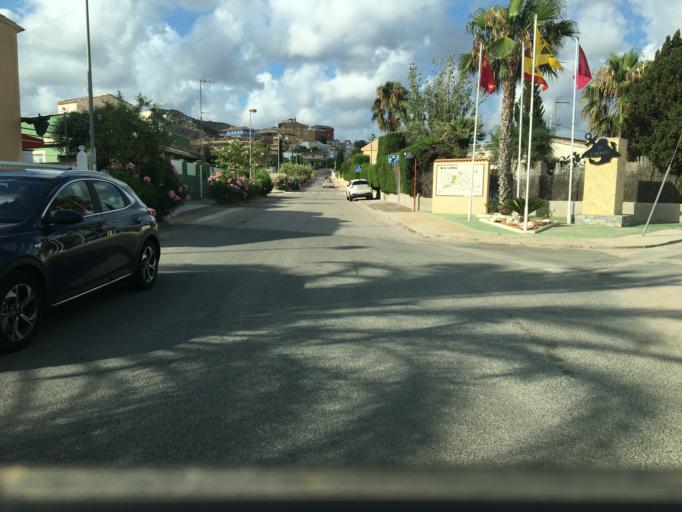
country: ES
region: Murcia
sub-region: Murcia
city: Los Alcazares
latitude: 37.6955
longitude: -0.8423
